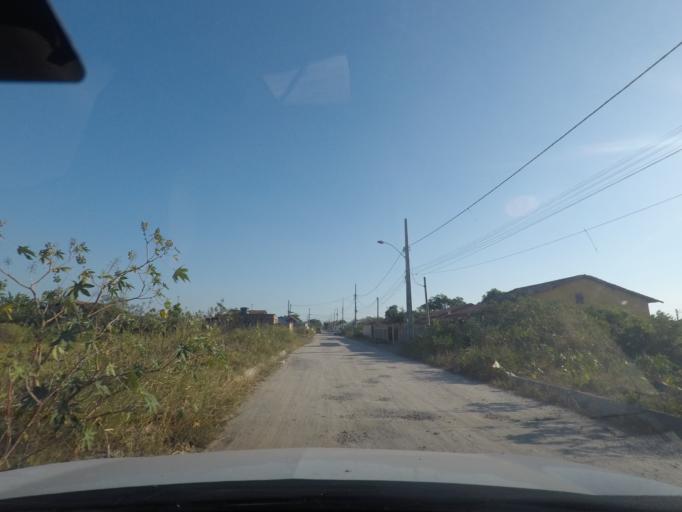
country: BR
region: Rio de Janeiro
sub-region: Marica
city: Marica
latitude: -22.9632
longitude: -42.9360
